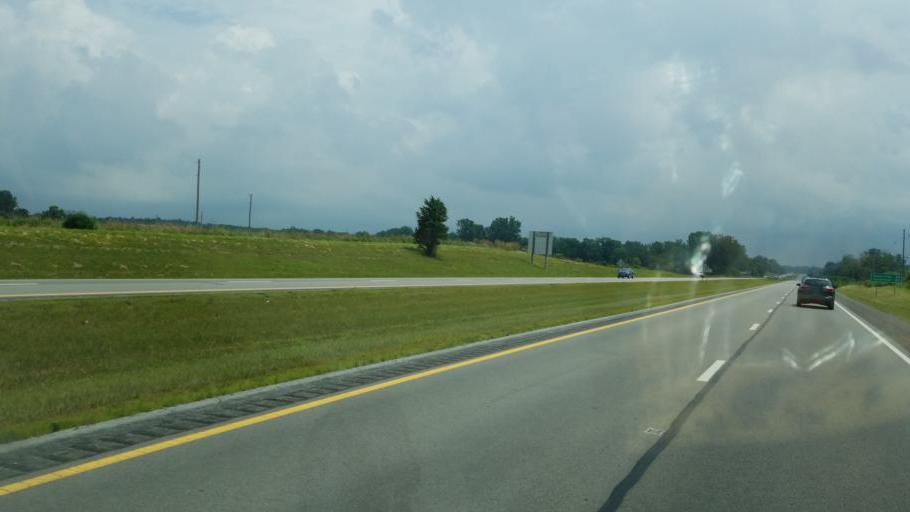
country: US
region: Ohio
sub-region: Logan County
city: Bellefontaine
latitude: 40.4252
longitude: -83.7990
